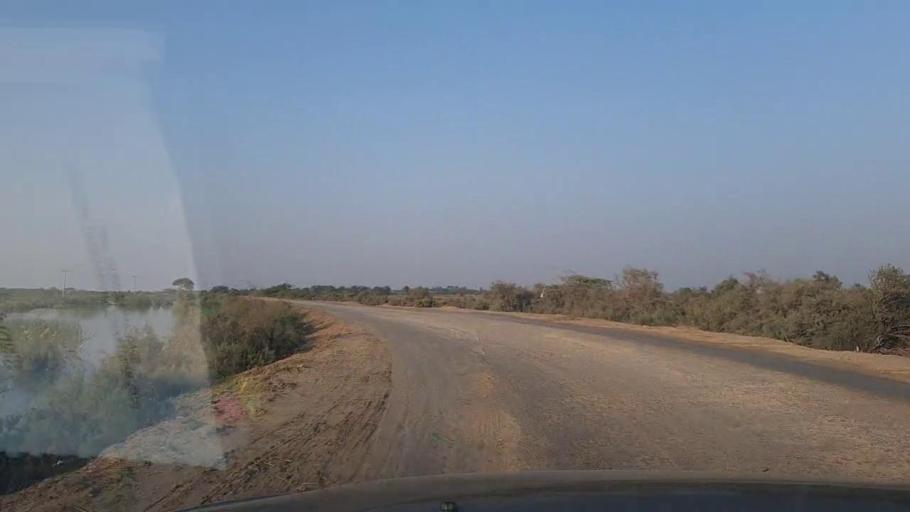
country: PK
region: Sindh
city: Keti Bandar
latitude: 24.2771
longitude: 67.5876
